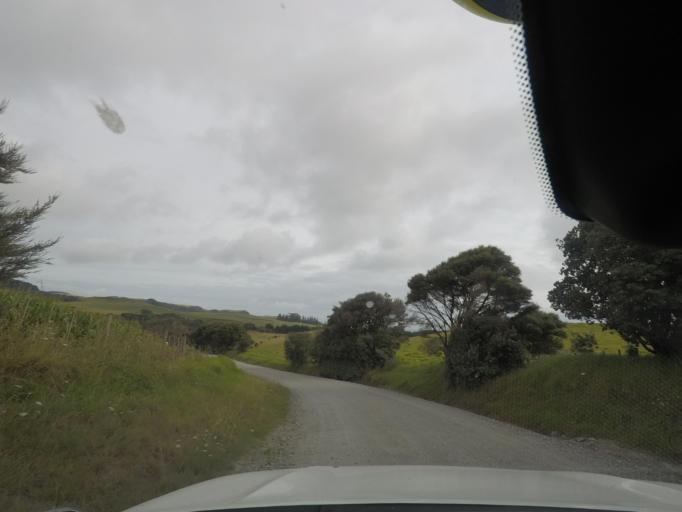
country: NZ
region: Auckland
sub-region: Auckland
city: Parakai
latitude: -36.4740
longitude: 174.2576
